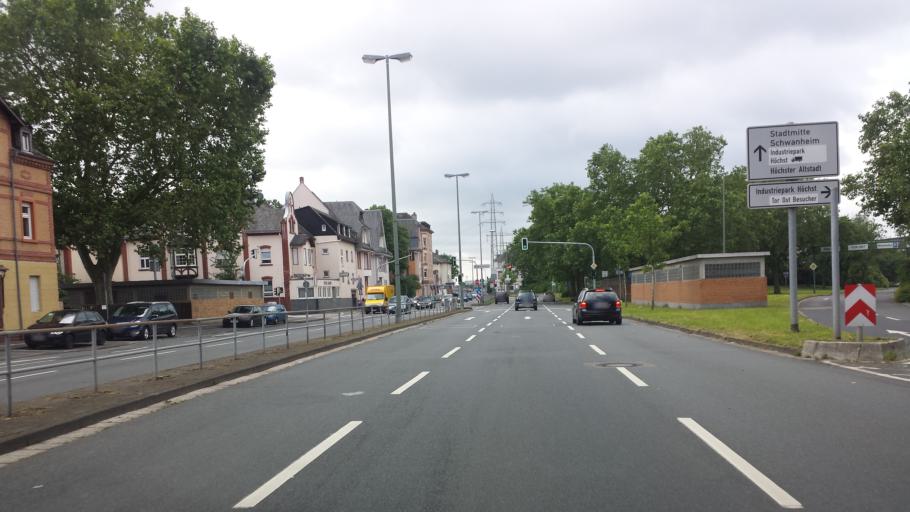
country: DE
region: Hesse
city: Sulzbach
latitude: 50.1002
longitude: 8.5398
